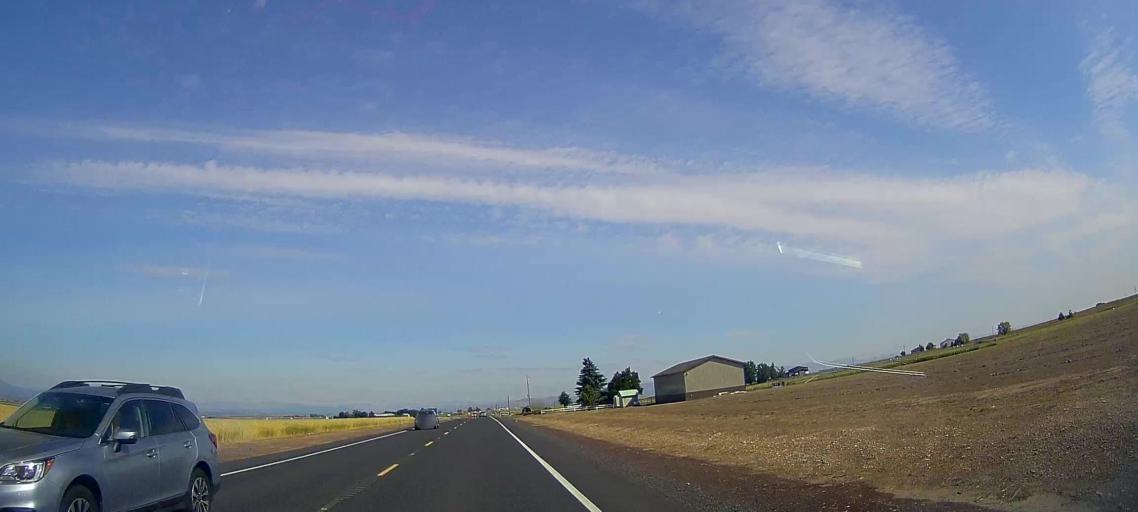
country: US
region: Oregon
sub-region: Jefferson County
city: Madras
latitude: 44.6741
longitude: -121.1427
